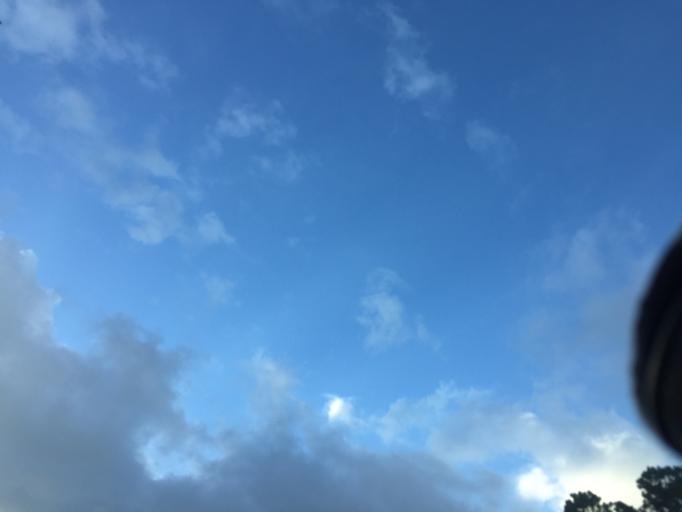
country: US
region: Georgia
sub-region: Chatham County
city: Tybee Island
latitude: 32.0191
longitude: -80.8522
